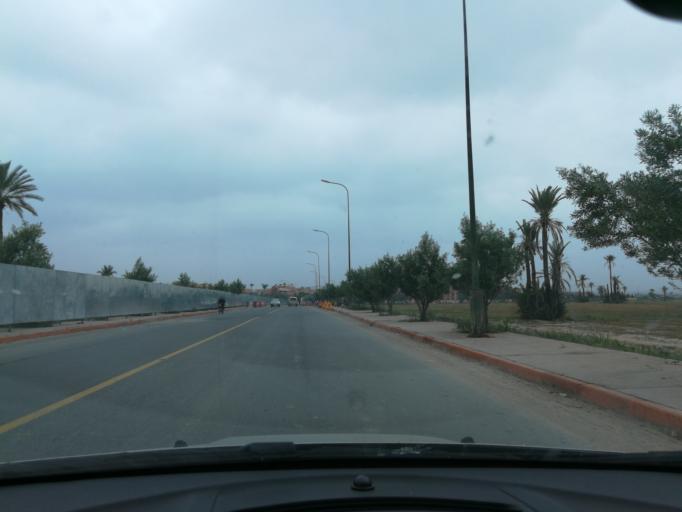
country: MA
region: Marrakech-Tensift-Al Haouz
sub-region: Marrakech
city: Marrakesh
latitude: 31.6715
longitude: -7.9982
